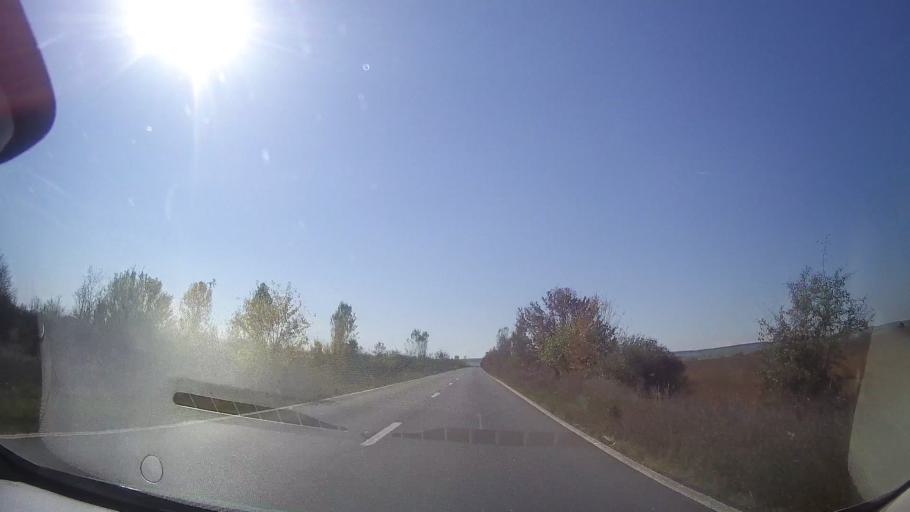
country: RO
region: Timis
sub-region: Comuna Traian Vuia
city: Traian Vuia
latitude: 45.7731
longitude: 22.0454
